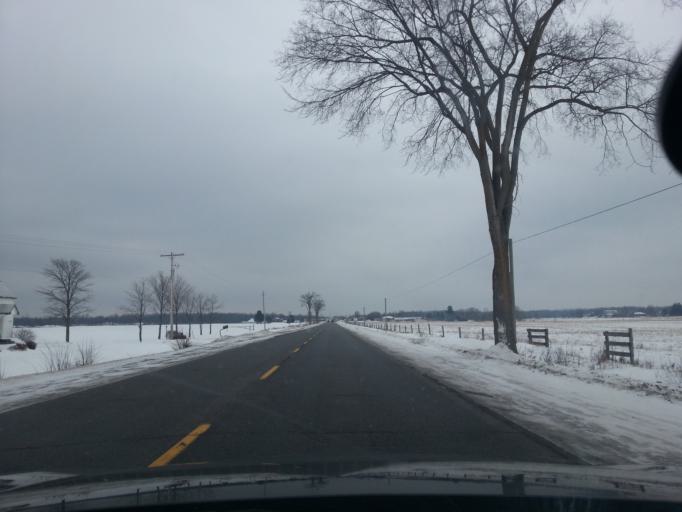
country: CA
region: Ontario
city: Bells Corners
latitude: 45.3221
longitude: -76.0429
